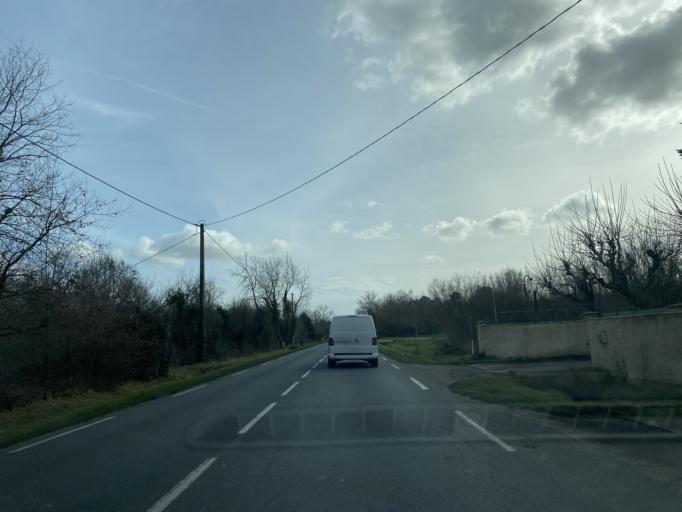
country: FR
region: Aquitaine
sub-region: Departement de la Gironde
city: Le Taillan-Medoc
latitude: 44.9264
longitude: -0.6775
